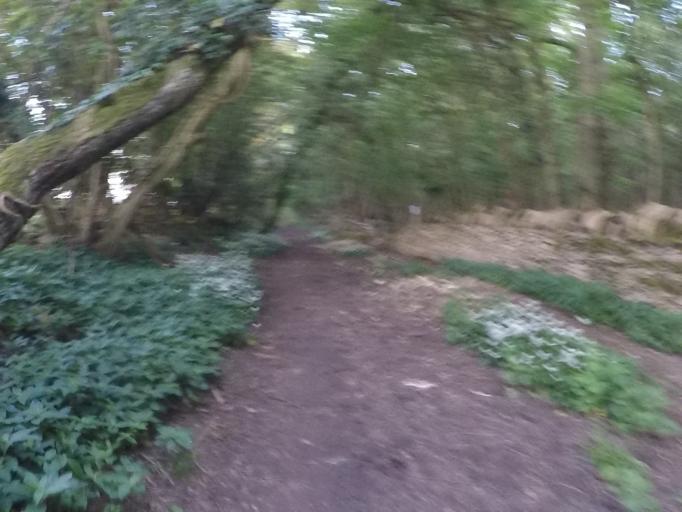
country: GB
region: England
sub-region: Oxfordshire
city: Witney
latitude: 51.8270
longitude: -1.4978
